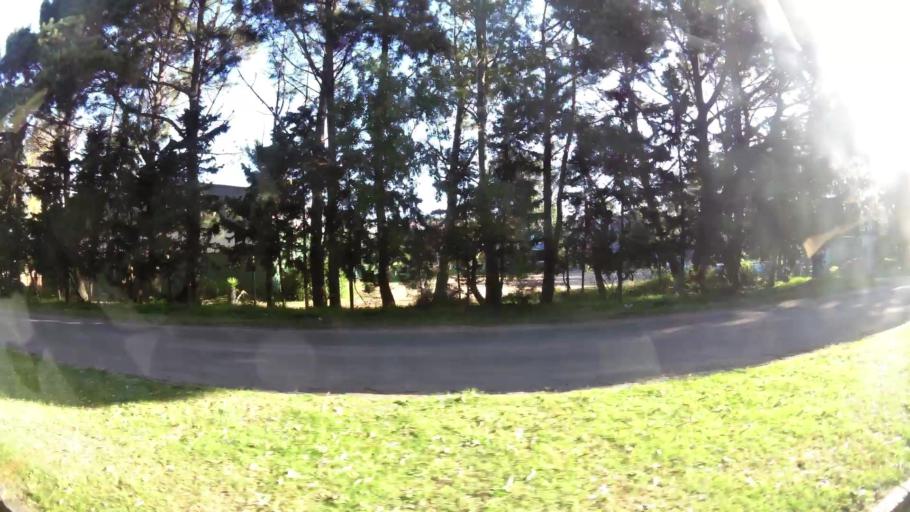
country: UY
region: Canelones
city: Paso de Carrasco
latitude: -34.8701
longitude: -56.0457
